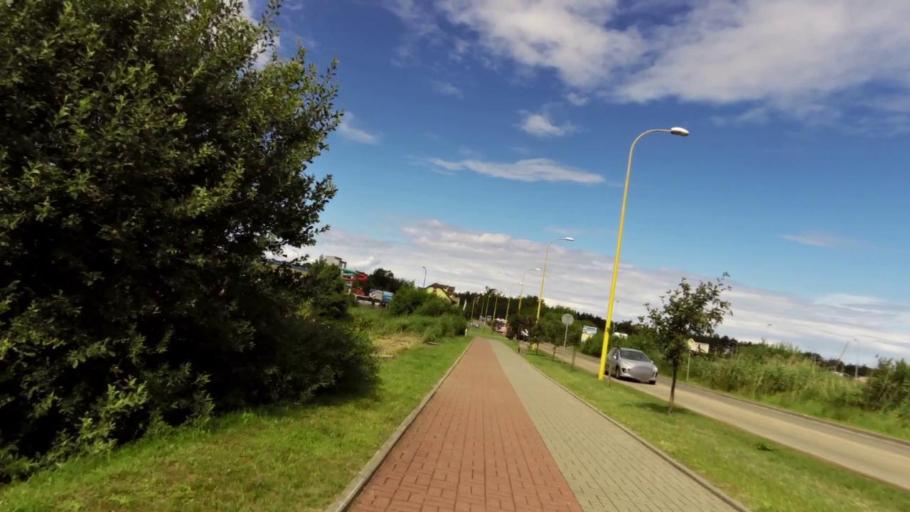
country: PL
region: West Pomeranian Voivodeship
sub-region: Powiat slawienski
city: Darlowo
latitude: 54.4437
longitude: 16.3992
